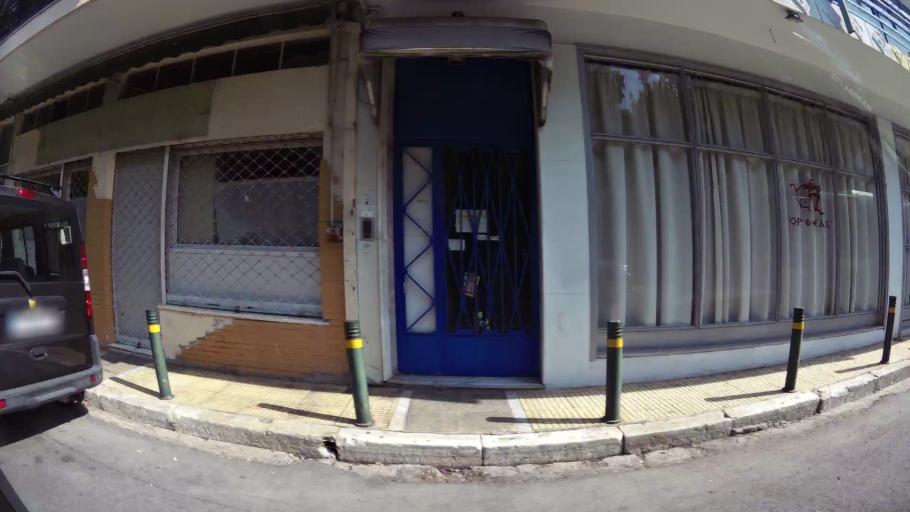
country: GR
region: Attica
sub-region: Nomarchia Athinas
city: Athens
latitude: 37.9958
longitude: 23.7161
